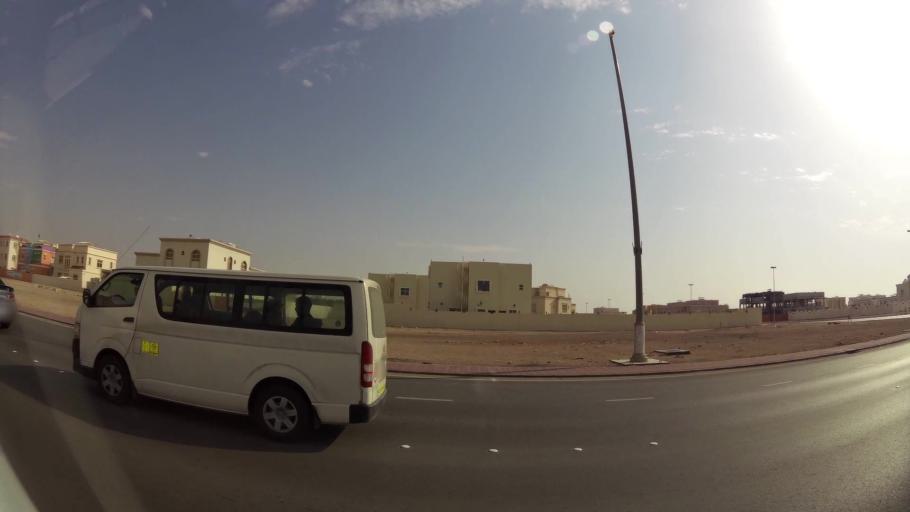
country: AE
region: Abu Dhabi
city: Abu Dhabi
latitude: 24.3254
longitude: 54.5624
